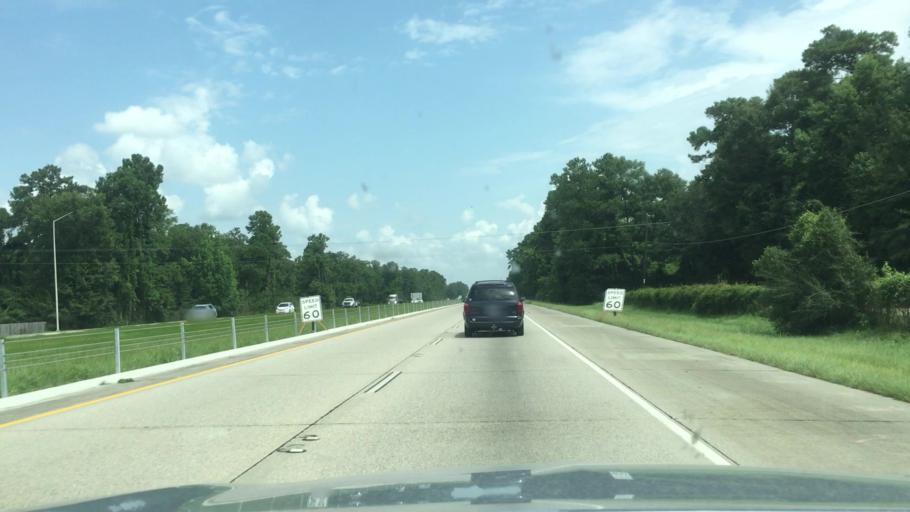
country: US
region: Louisiana
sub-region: Saint Tammany Parish
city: Pearl River
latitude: 30.3228
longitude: -89.7375
